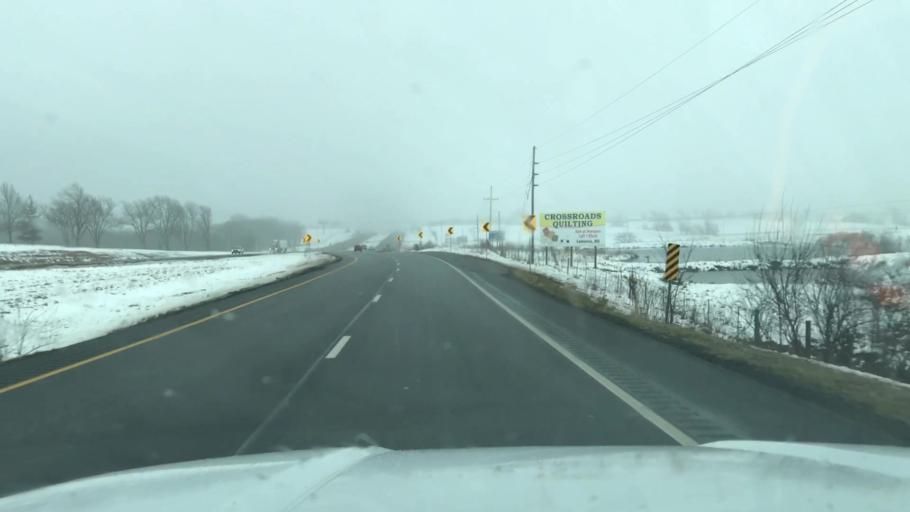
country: US
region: Missouri
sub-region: Clinton County
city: Cameron
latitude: 39.7538
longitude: -94.2695
